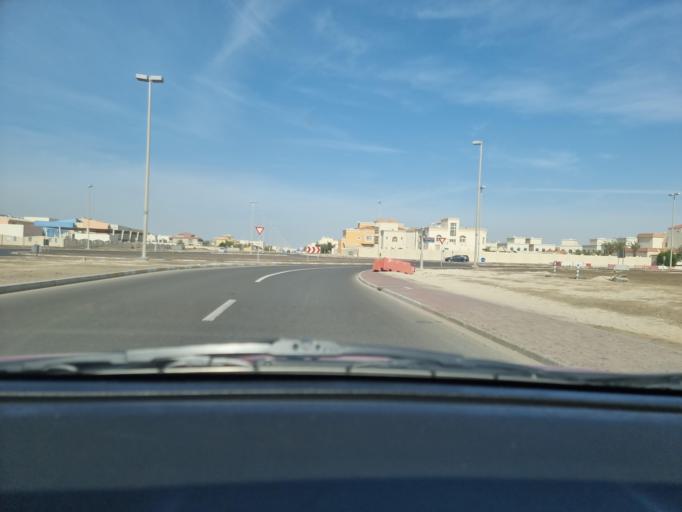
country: AE
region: Abu Dhabi
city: Abu Dhabi
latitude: 24.3153
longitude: 54.5619
